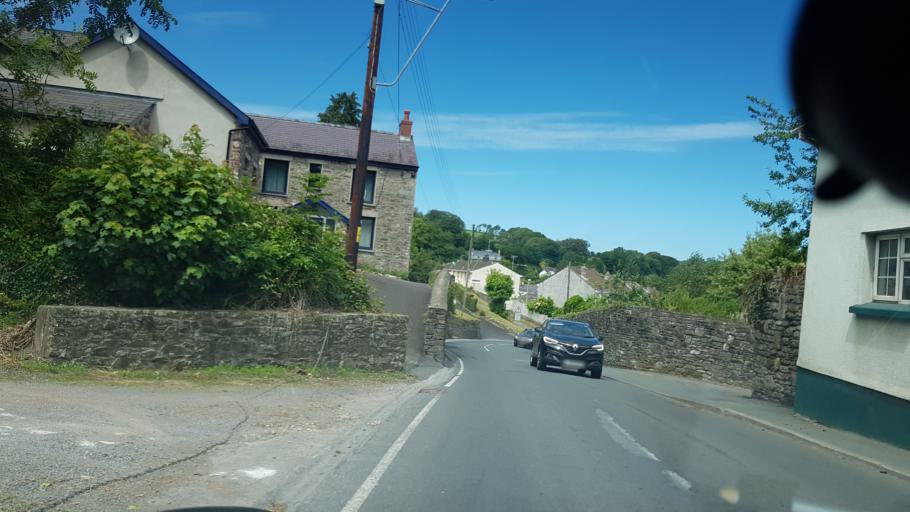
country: GB
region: Wales
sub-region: Carmarthenshire
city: Saint Clears
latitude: 51.7671
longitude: -4.4632
